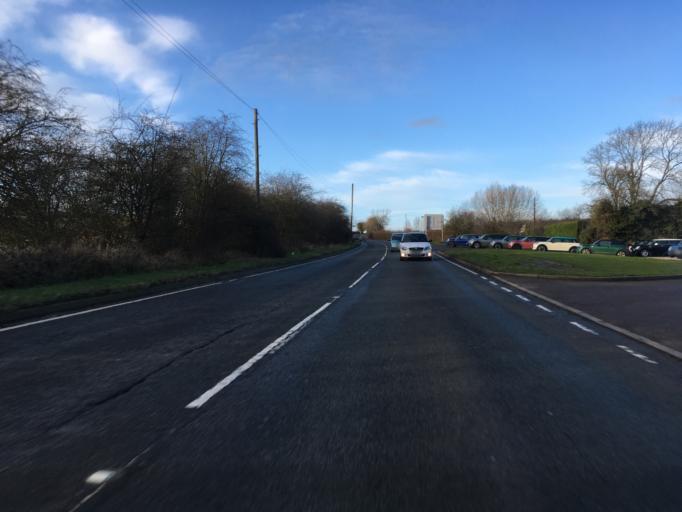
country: GB
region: England
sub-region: Warwickshire
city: Stratford-upon-Avon
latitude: 52.2152
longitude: -1.7279
